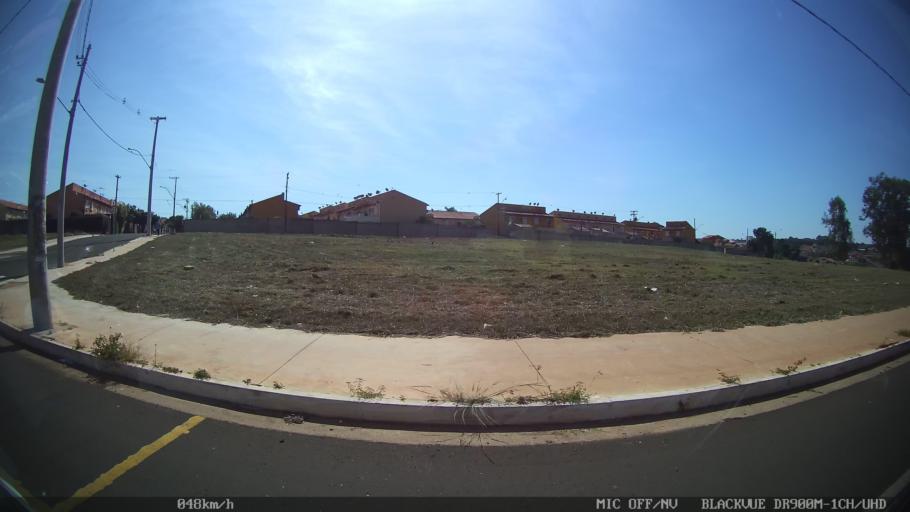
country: BR
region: Sao Paulo
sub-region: Sao Jose Do Rio Preto
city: Sao Jose do Rio Preto
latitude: -20.7894
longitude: -49.4171
